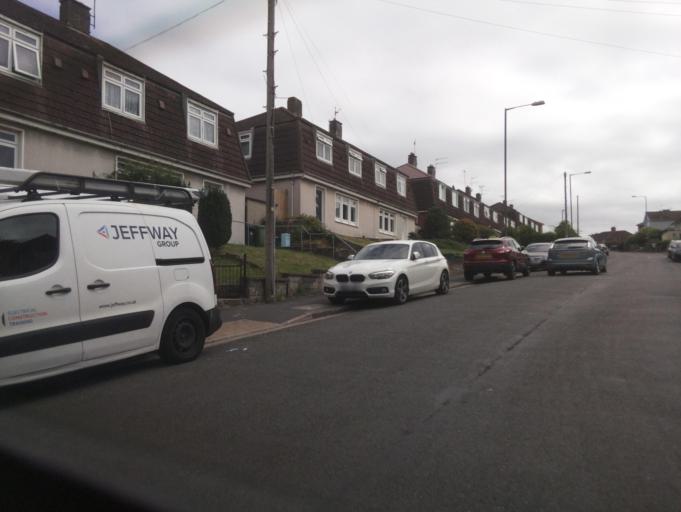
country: GB
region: England
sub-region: Bristol
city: Bristol
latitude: 51.4307
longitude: -2.5847
